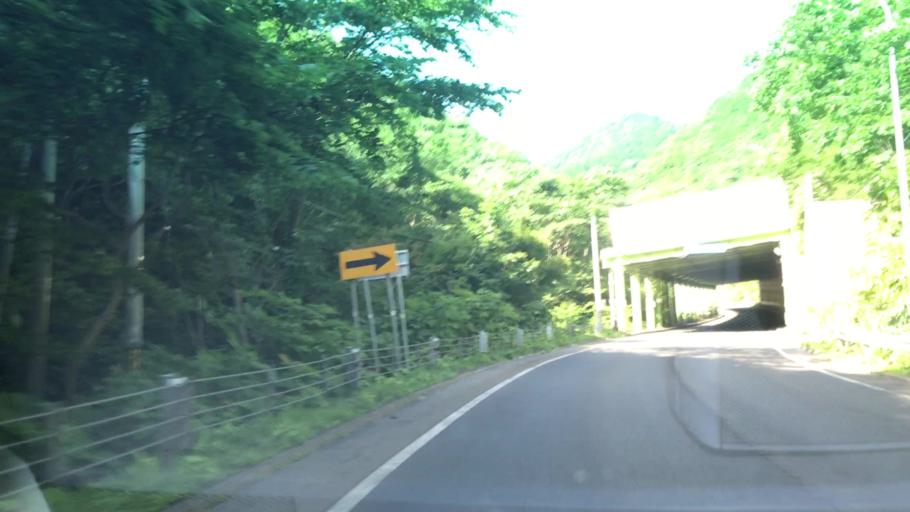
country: JP
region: Hokkaido
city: Iwanai
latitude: 43.0315
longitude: 140.6752
